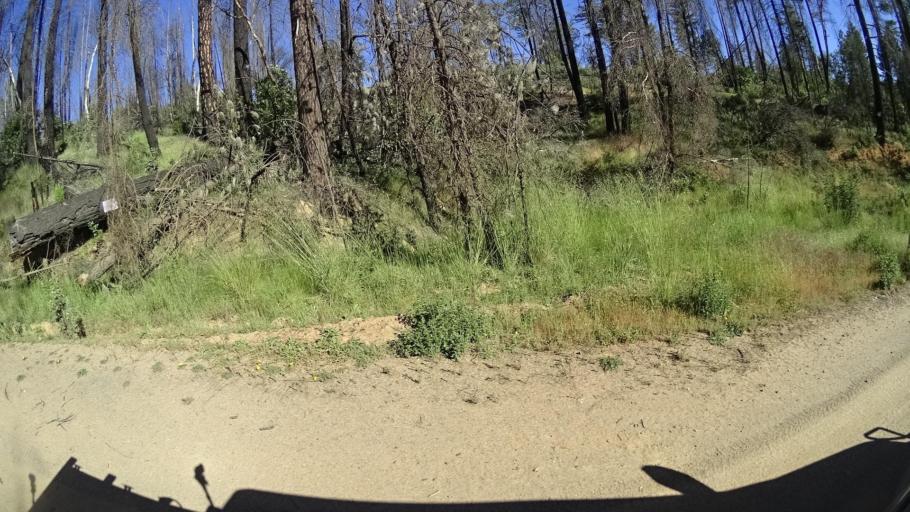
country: US
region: California
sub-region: Lake County
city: Upper Lake
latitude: 39.3930
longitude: -122.9759
